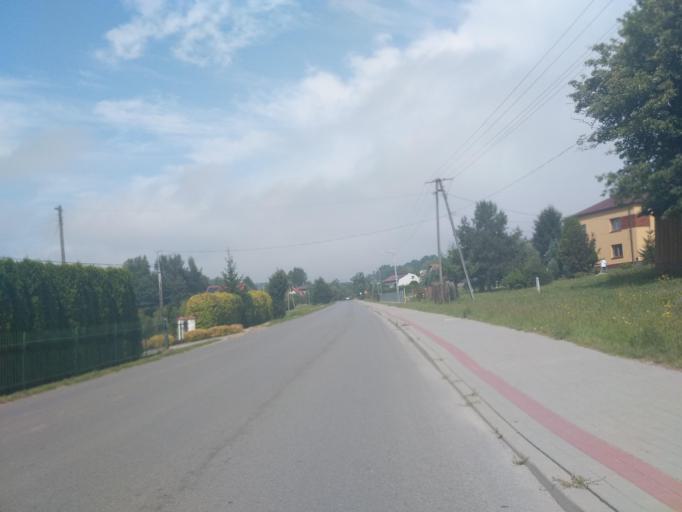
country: PL
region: Subcarpathian Voivodeship
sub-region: Powiat rzeszowski
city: Chmielnik
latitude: 49.9867
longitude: 22.1123
